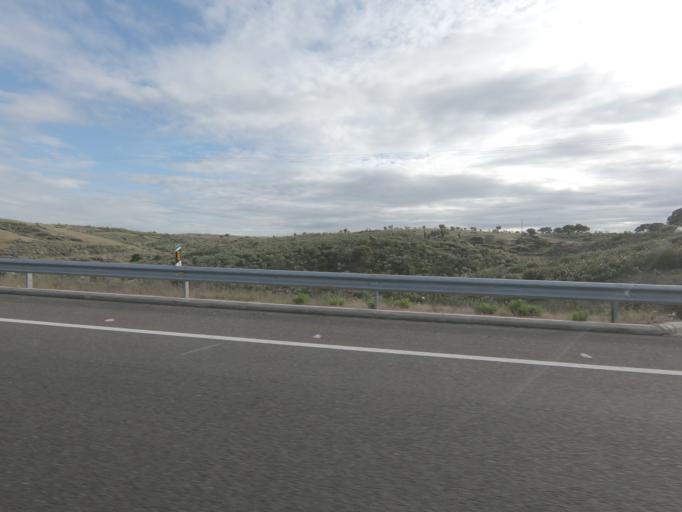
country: ES
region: Extremadura
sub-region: Provincia de Caceres
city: Casas de Don Gomez
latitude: 40.0256
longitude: -6.6051
